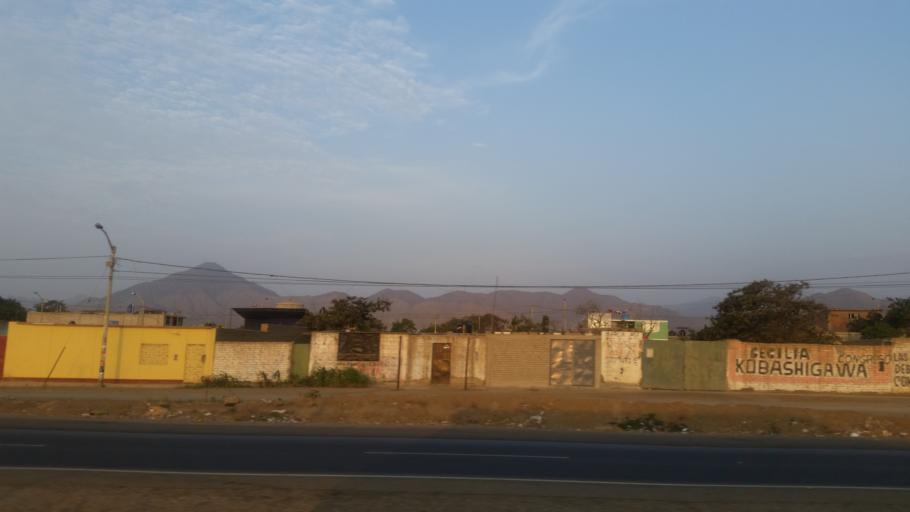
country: PE
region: La Libertad
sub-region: Ascope
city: Chicama
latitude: -7.8653
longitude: -79.1375
